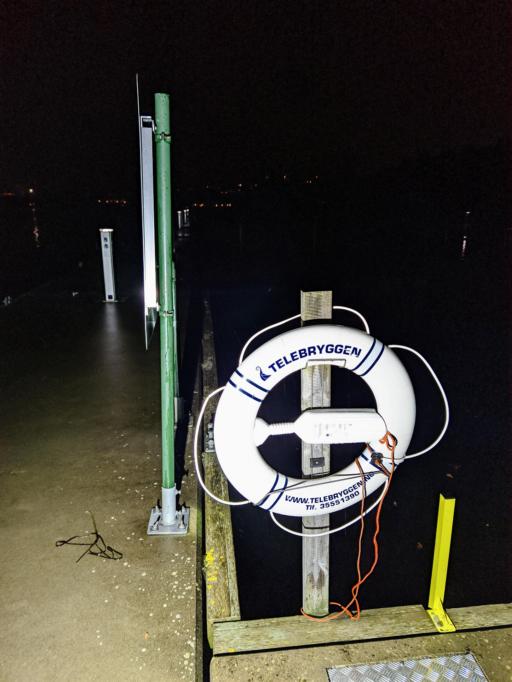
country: NO
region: Vest-Agder
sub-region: Sogne
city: Tangvall
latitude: 58.0729
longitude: 7.8204
